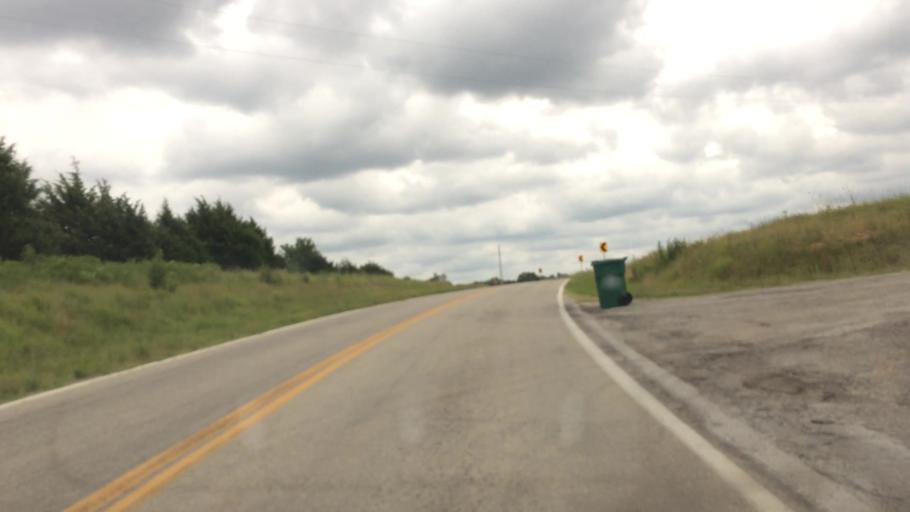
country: US
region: Missouri
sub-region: Greene County
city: Strafford
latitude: 37.3009
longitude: -93.1755
